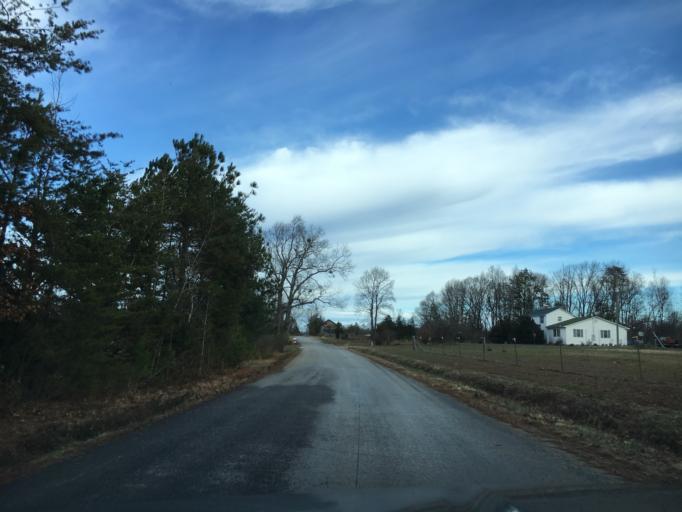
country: US
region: Virginia
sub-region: Nottoway County
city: Crewe
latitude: 37.2432
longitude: -78.2270
